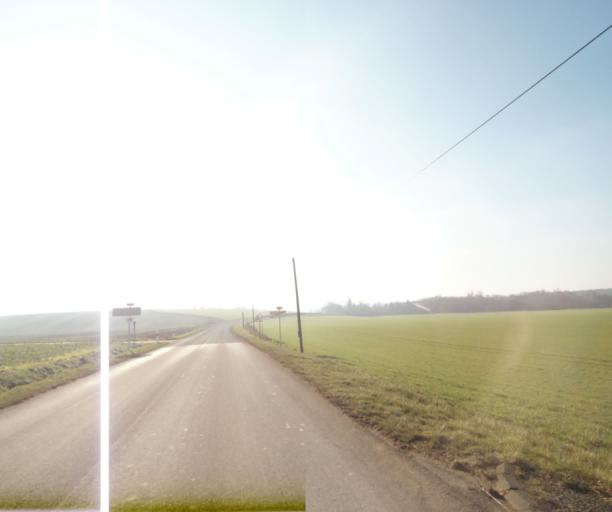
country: FR
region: Champagne-Ardenne
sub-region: Departement de la Haute-Marne
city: Wassy
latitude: 48.4526
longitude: 4.9614
